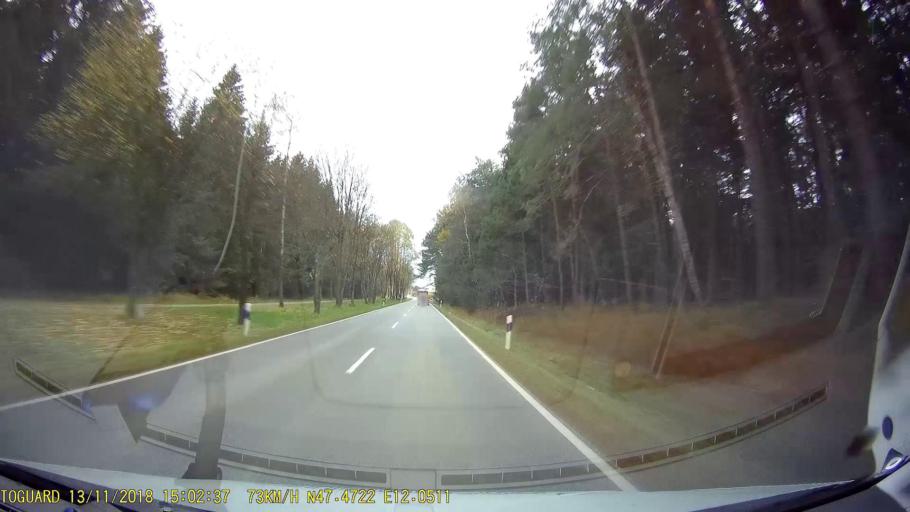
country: DE
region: Bavaria
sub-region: Upper Bavaria
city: Raubling
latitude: 47.7871
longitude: 12.0848
